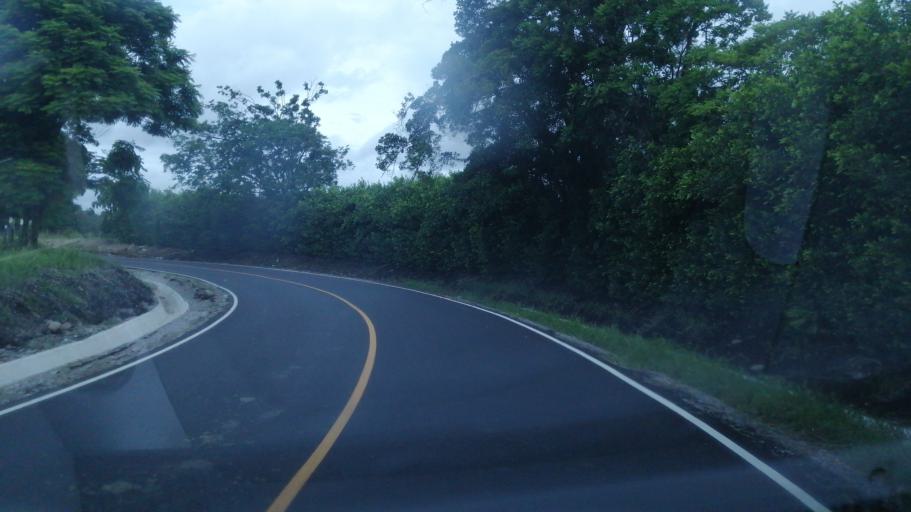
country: PA
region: Chiriqui
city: Alanje
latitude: 8.4322
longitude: -82.5193
